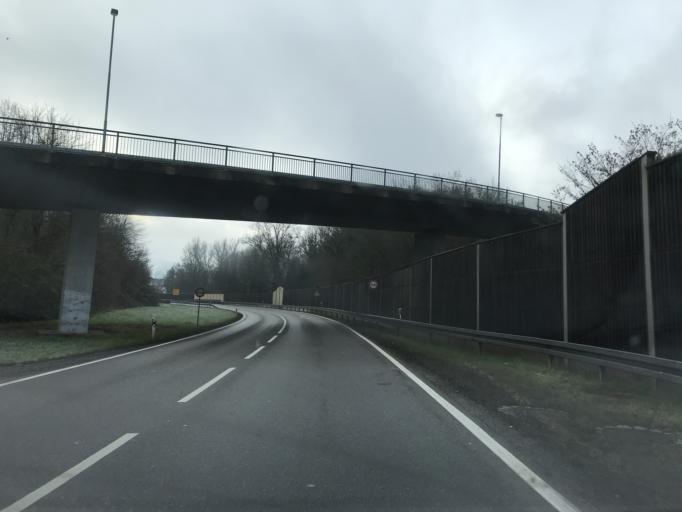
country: DE
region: Baden-Wuerttemberg
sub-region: Freiburg Region
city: Wehr
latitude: 47.6271
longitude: 7.8973
